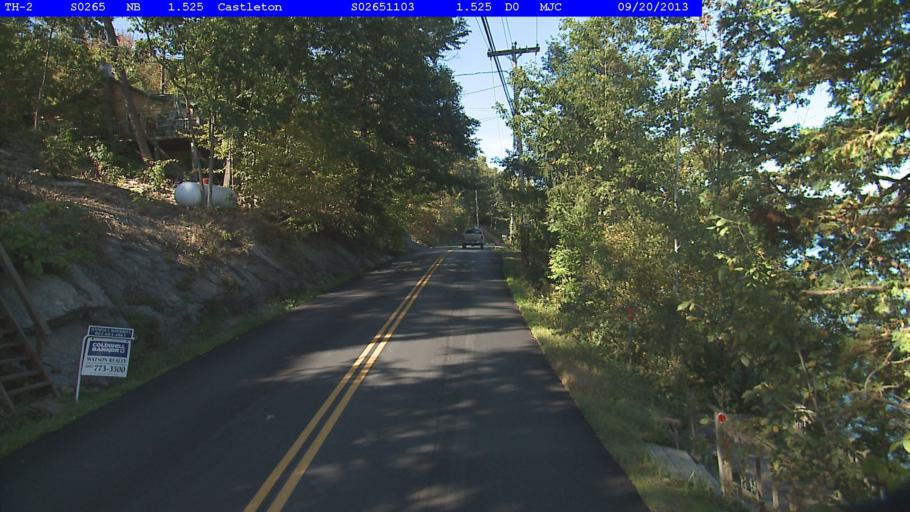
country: US
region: Vermont
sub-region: Rutland County
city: Fair Haven
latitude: 43.6247
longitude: -73.2330
